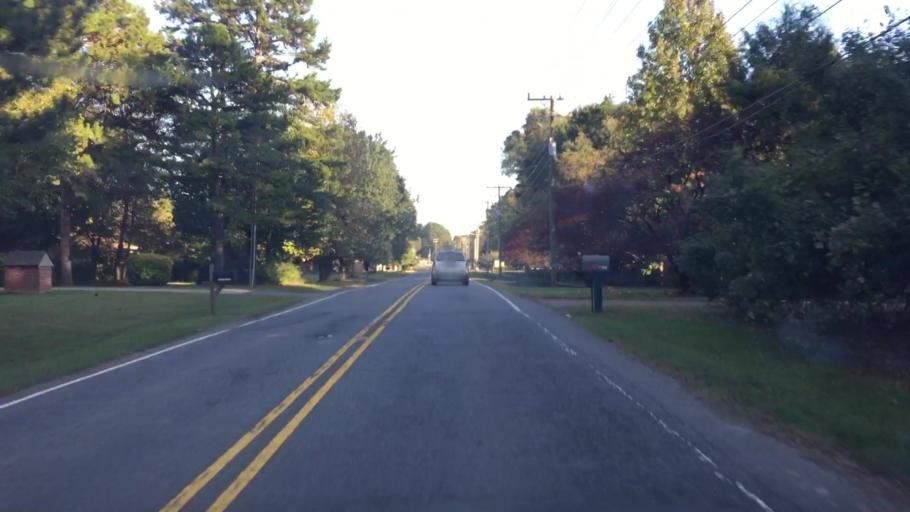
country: US
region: North Carolina
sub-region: Iredell County
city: Mooresville
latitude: 35.5581
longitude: -80.8468
